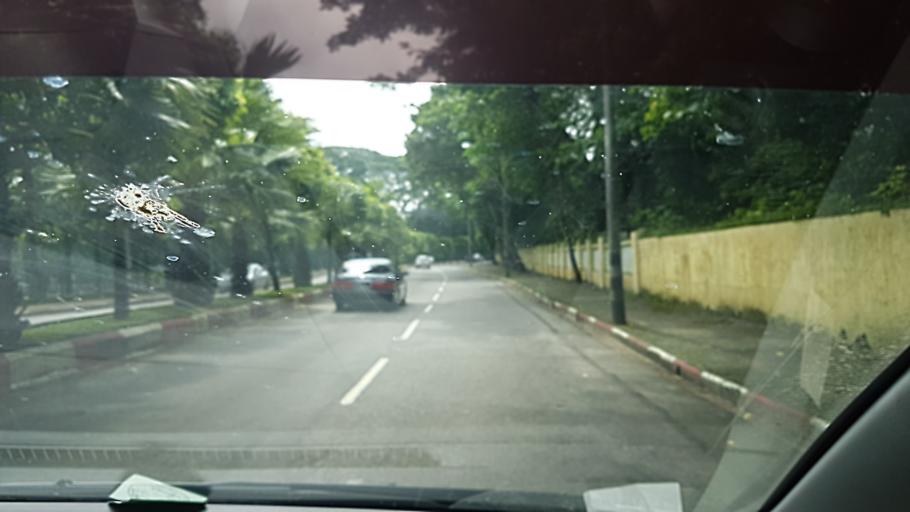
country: MM
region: Yangon
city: Yangon
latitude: 16.7951
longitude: 96.1579
